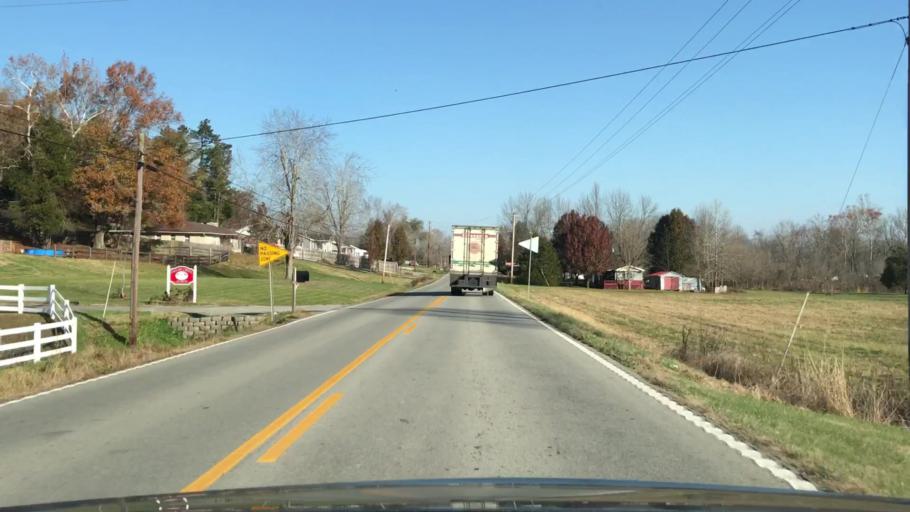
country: US
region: Kentucky
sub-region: Grayson County
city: Leitchfield
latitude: 37.4546
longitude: -86.2907
